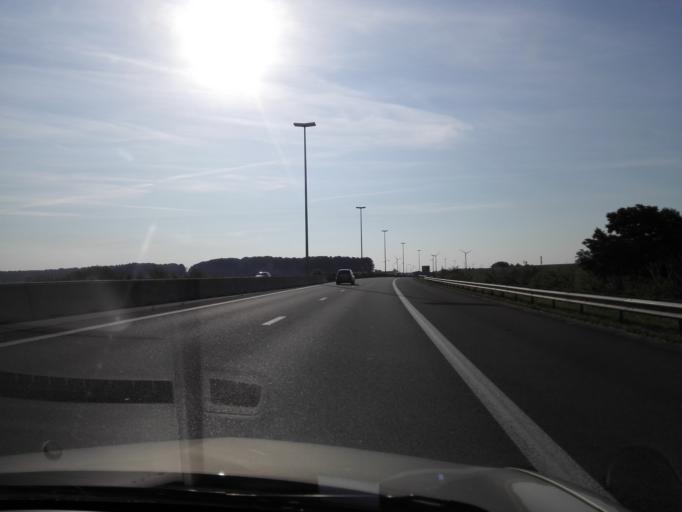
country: BE
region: Flanders
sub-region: Provincie Vlaams-Brabant
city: Bekkevoort
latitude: 50.9563
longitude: 4.9879
